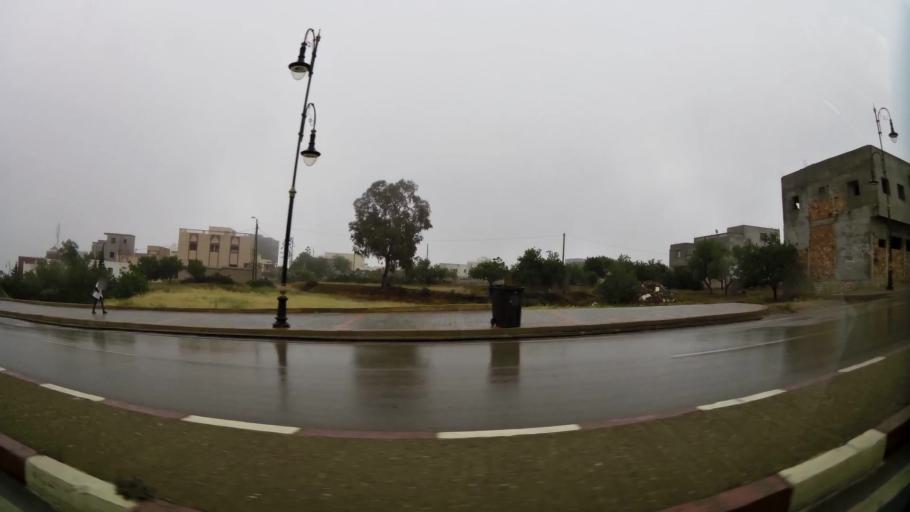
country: MA
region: Taza-Al Hoceima-Taounate
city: Tirhanimine
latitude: 35.1963
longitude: -3.9044
